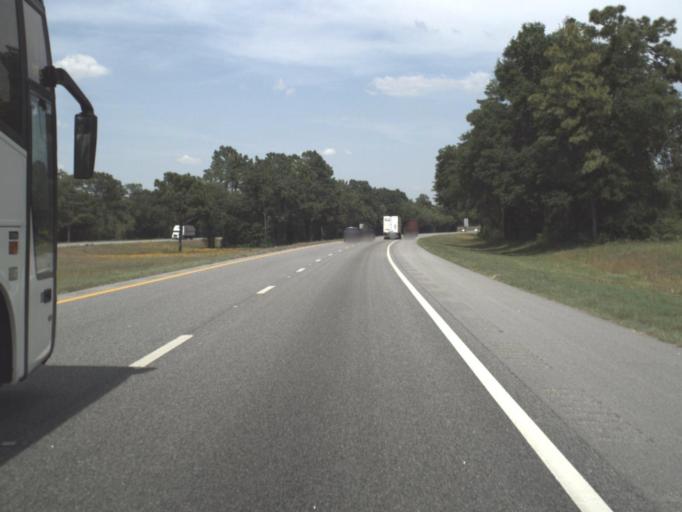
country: US
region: Florida
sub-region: Suwannee County
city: Live Oak
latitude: 30.3465
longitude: -83.0844
